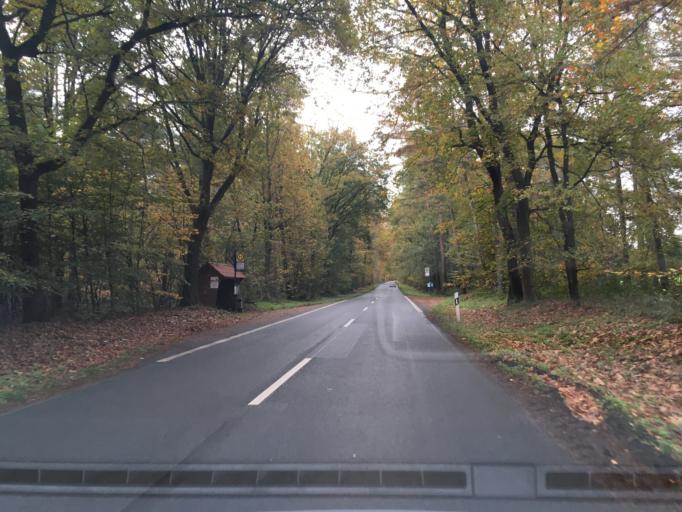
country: DE
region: North Rhine-Westphalia
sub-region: Regierungsbezirk Munster
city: Heiden
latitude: 51.8234
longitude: 6.9750
